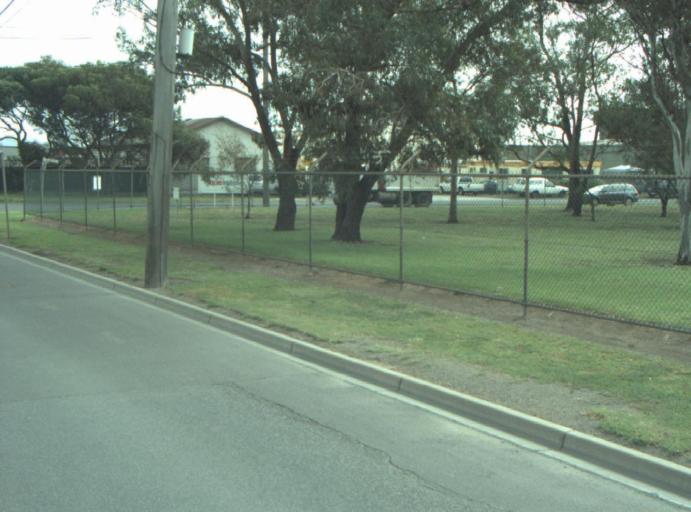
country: AU
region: Victoria
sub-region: Greater Geelong
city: Bell Park
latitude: -38.0884
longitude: 144.3769
